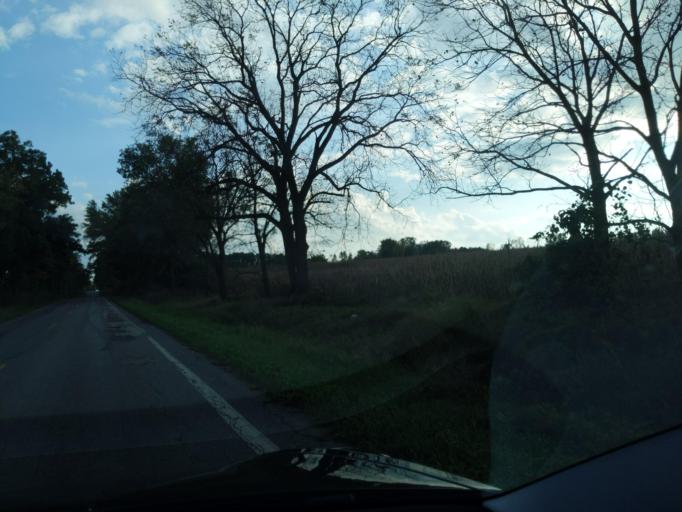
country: US
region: Michigan
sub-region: Jackson County
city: Jackson
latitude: 42.2801
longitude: -84.4831
